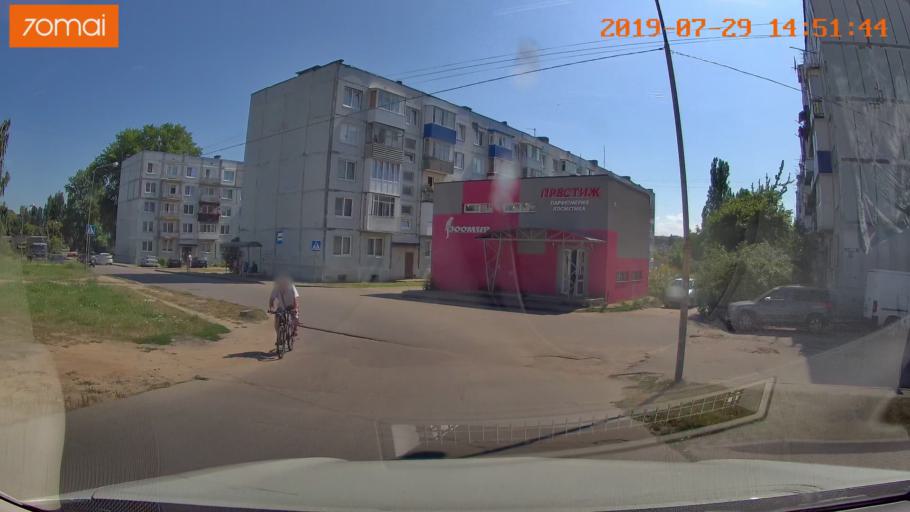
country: RU
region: Kaliningrad
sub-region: Gorod Kaliningrad
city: Baltiysk
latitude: 54.6633
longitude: 19.9067
